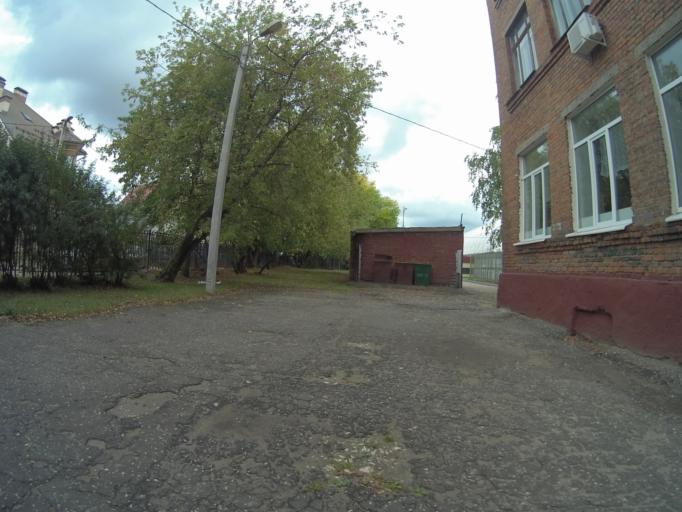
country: RU
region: Vladimir
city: Vladimir
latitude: 56.1162
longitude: 40.3615
